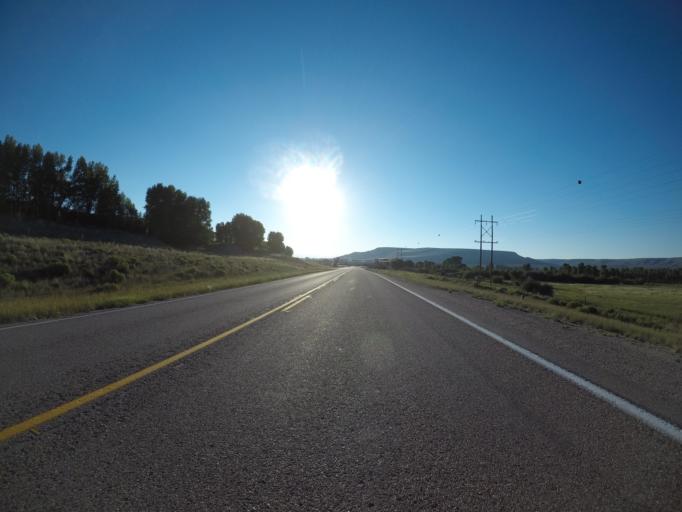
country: US
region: Wyoming
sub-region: Sublette County
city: Marbleton
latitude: 42.5698
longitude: -109.9543
